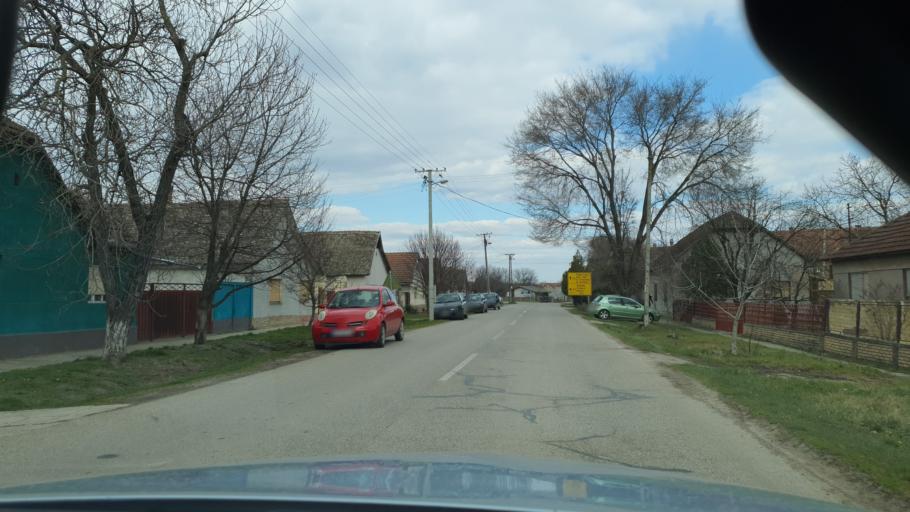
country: RS
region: Autonomna Pokrajina Vojvodina
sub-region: Zapadnobacki Okrug
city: Odzaci
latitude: 45.4485
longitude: 19.3304
